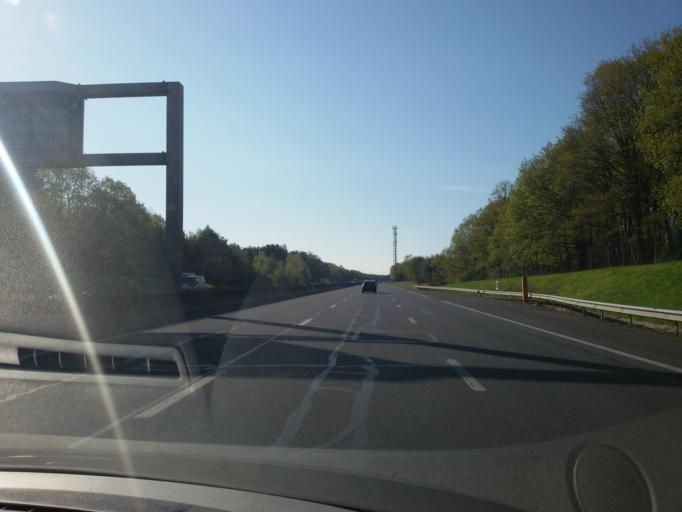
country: FR
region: Ile-de-France
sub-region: Departement de Seine-et-Marne
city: Bagneaux-sur-Loing
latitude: 48.2505
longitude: 2.7358
